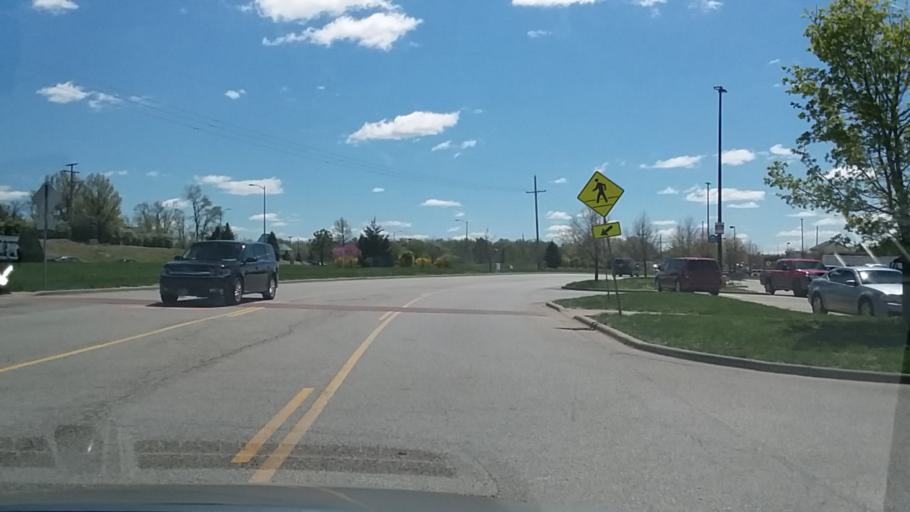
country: US
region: Kansas
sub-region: Johnson County
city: Olathe
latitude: 38.8868
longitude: -94.8357
